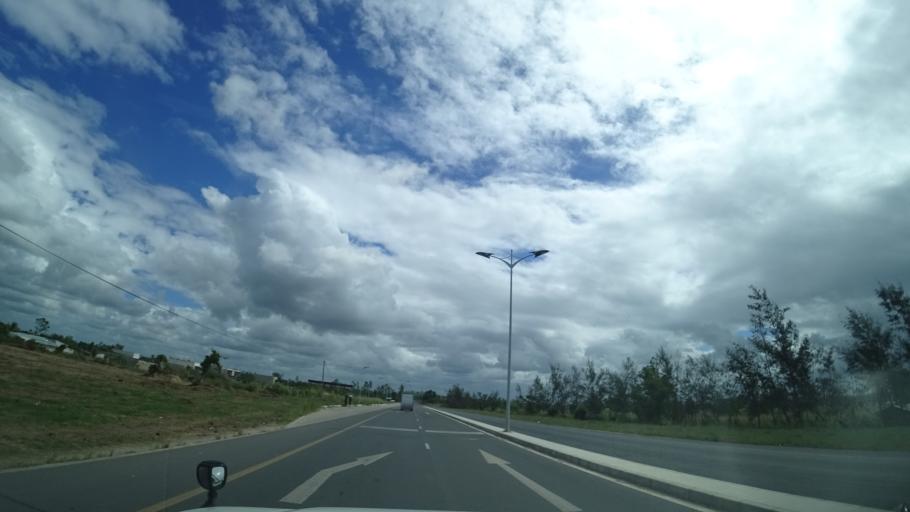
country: MZ
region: Sofala
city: Dondo
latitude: -19.5755
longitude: 34.7207
